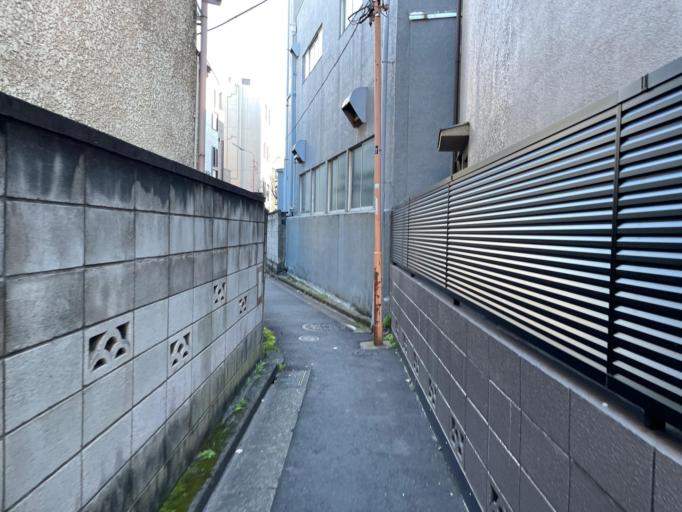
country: JP
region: Tokyo
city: Urayasu
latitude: 35.7266
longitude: 139.8187
